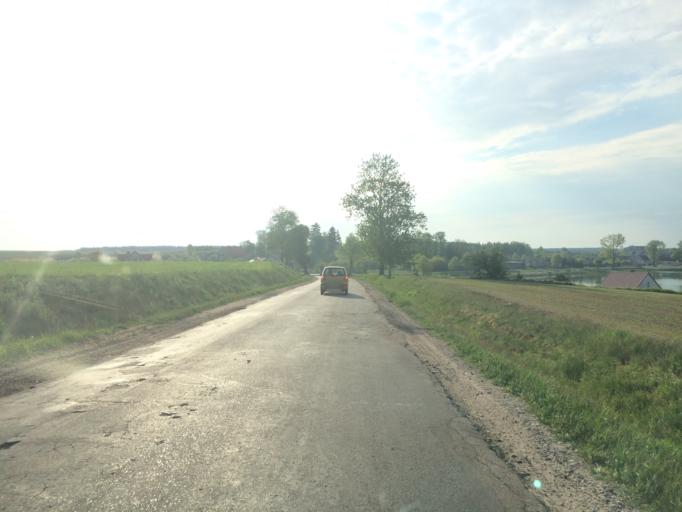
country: PL
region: Warmian-Masurian Voivodeship
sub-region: Powiat dzialdowski
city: Rybno
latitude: 53.3488
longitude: 19.9809
